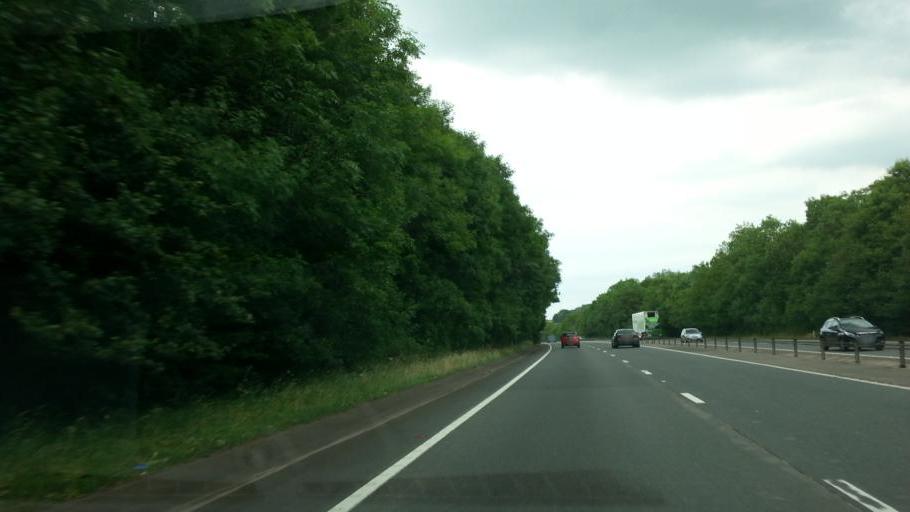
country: GB
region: Wales
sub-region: Monmouthshire
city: Llanbadoc
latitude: 51.6785
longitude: -2.8761
